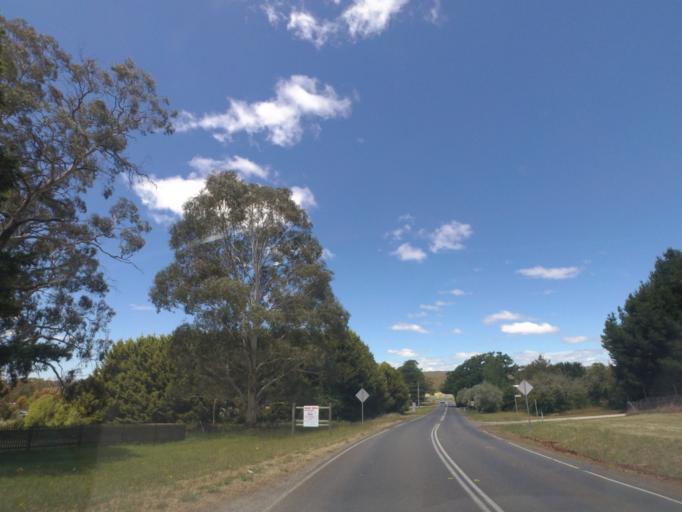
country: AU
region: Victoria
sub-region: Mount Alexander
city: Castlemaine
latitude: -37.2989
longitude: 144.2406
